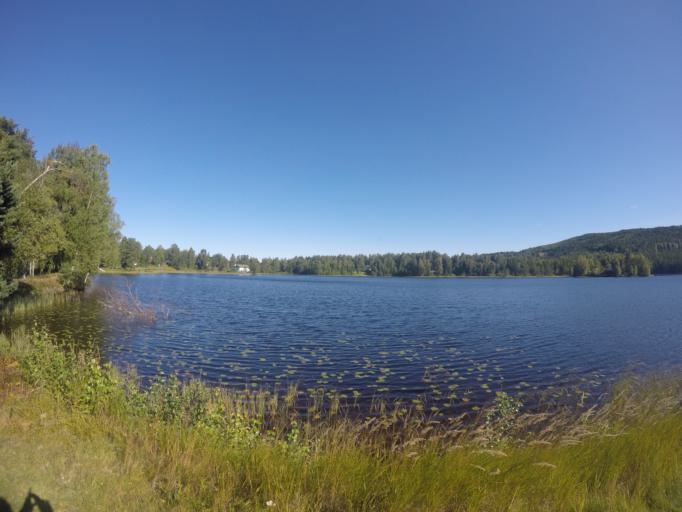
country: SE
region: Dalarna
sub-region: Ludvika Kommun
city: Ludvika
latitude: 60.1011
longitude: 15.1040
